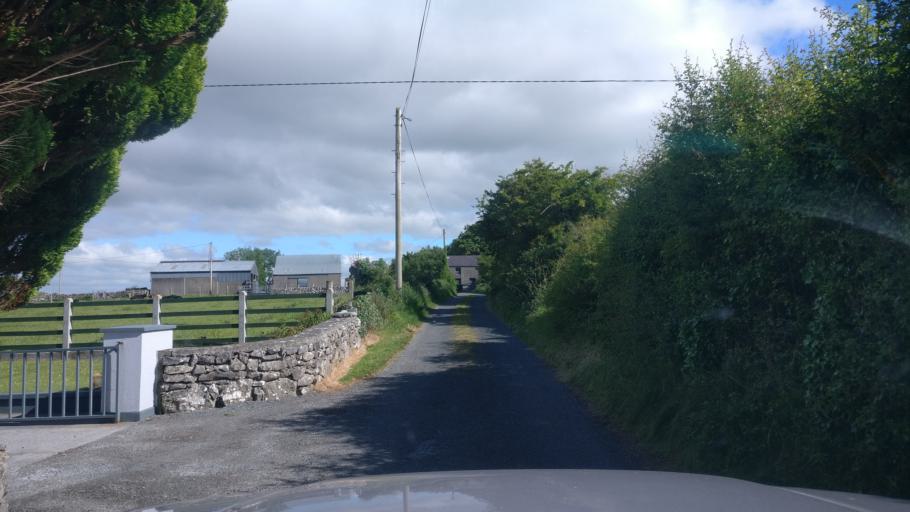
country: IE
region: Connaught
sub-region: County Galway
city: Loughrea
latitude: 53.2314
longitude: -8.5999
